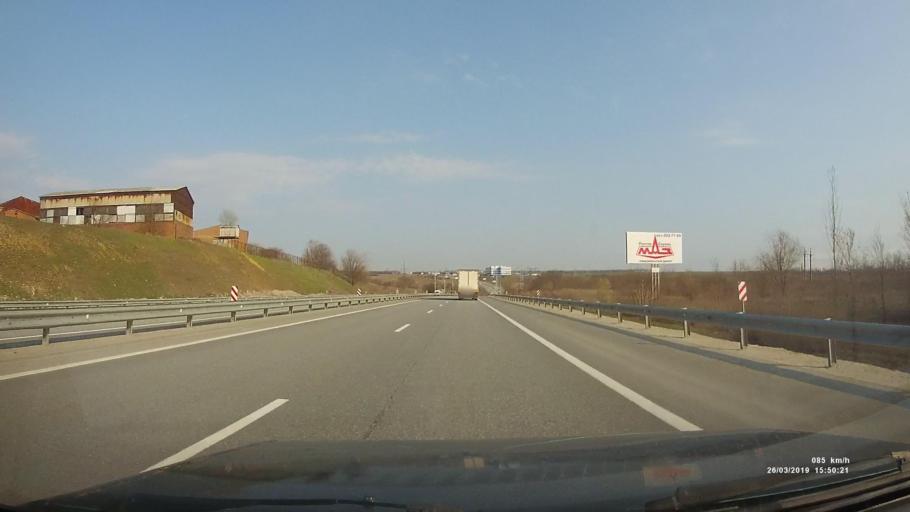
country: RU
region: Rostov
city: Chaltyr
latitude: 47.2737
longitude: 39.4858
